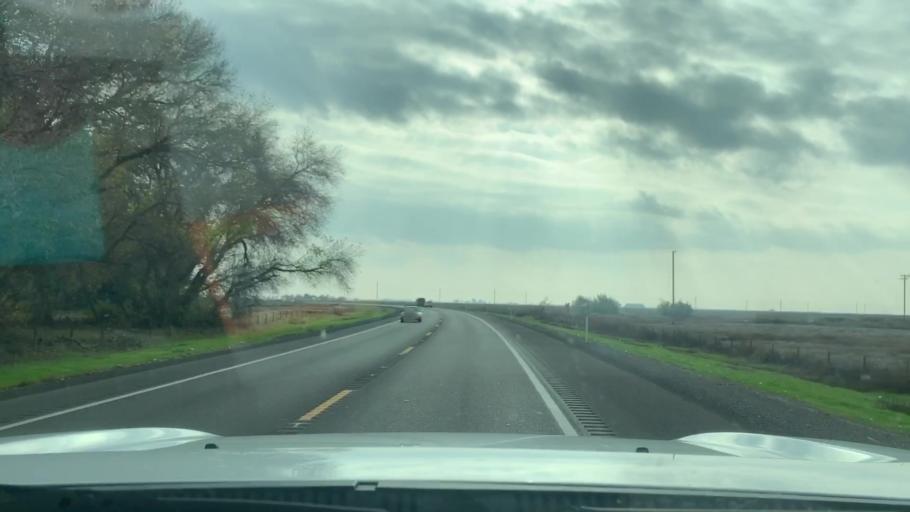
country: US
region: California
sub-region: Kings County
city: Stratford
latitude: 36.2472
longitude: -119.8148
